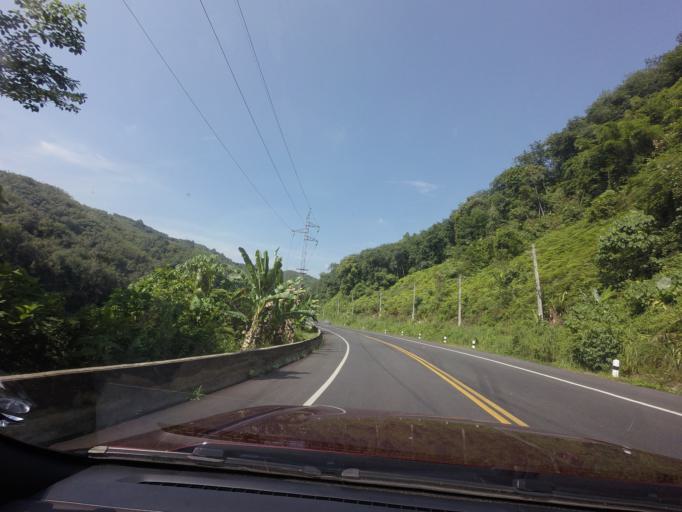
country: TH
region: Yala
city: Than To
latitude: 5.9687
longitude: 101.2005
